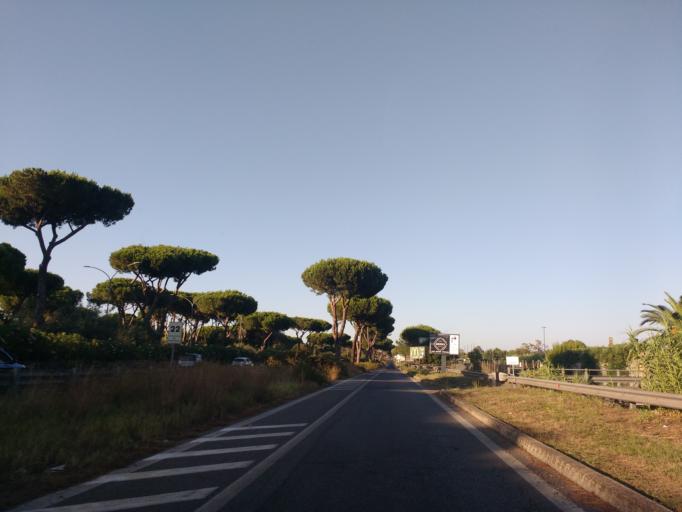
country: IT
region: Latium
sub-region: Citta metropolitana di Roma Capitale
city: Acilia-Castel Fusano-Ostia Antica
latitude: 41.7498
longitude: 12.3634
